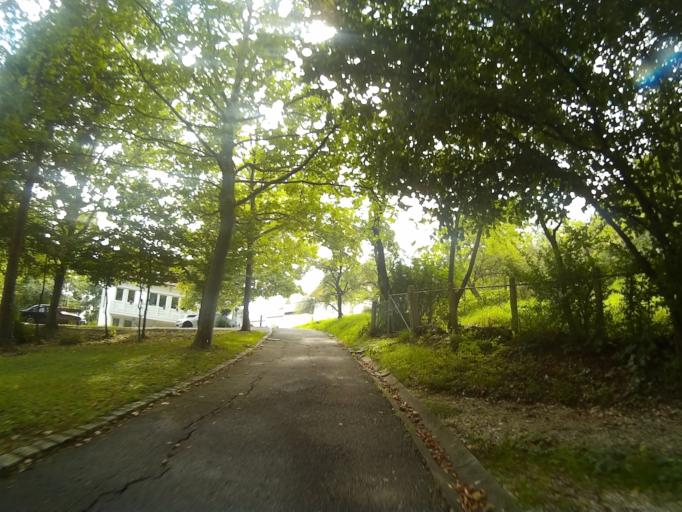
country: DE
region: Baden-Wuerttemberg
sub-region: Tuebingen Region
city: Pfullingen
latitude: 48.4743
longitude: 9.2194
